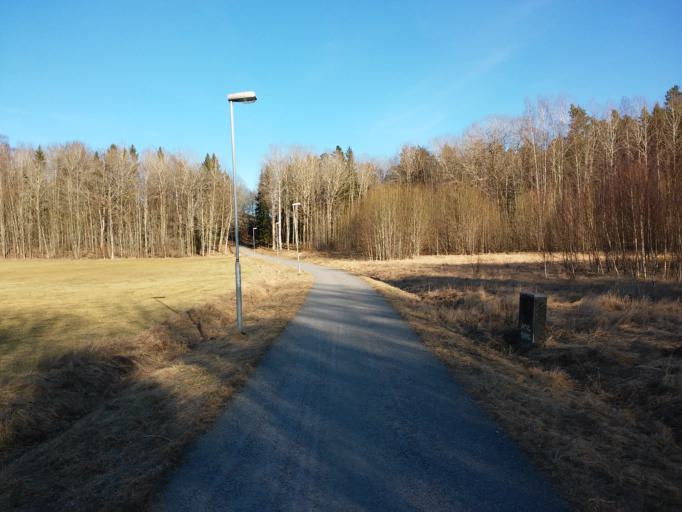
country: SE
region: Stockholm
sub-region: Osterakers Kommun
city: Akersberga
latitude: 59.4939
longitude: 18.3061
